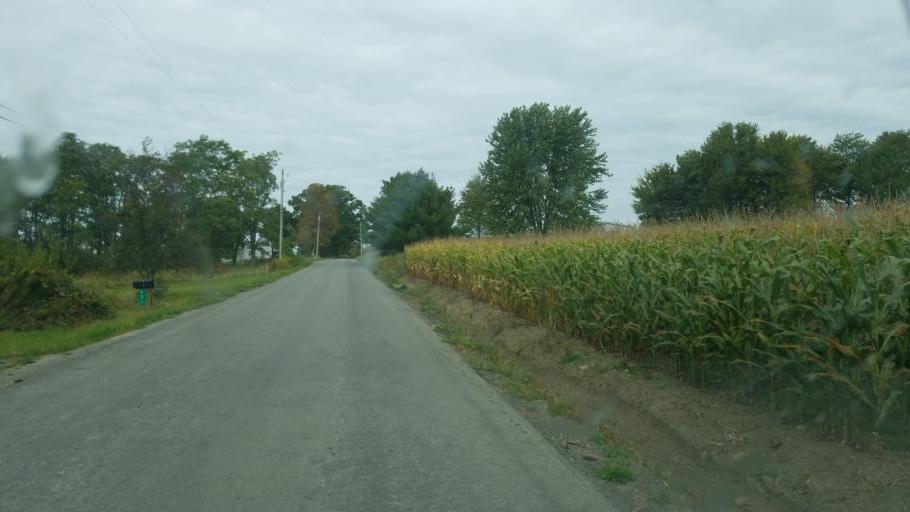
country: US
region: Pennsylvania
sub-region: Mercer County
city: Stoneboro
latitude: 41.3883
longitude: -80.2441
